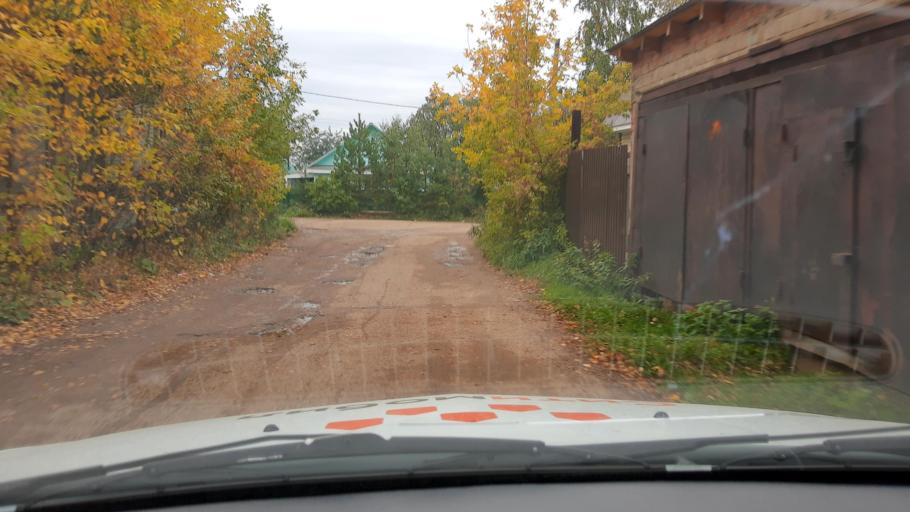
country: RU
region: Bashkortostan
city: Ufa
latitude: 54.8352
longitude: 56.1507
